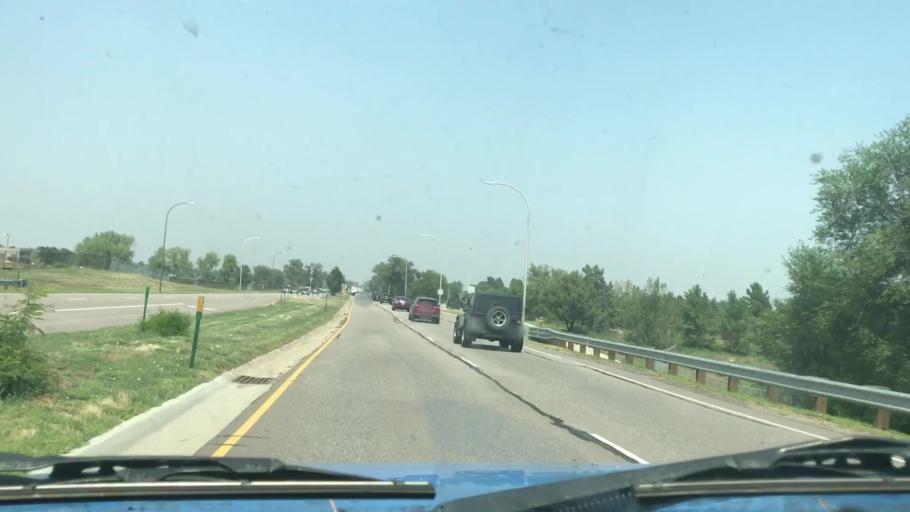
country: US
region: Colorado
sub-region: Jefferson County
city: Lakewood
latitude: 39.7171
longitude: -105.1097
